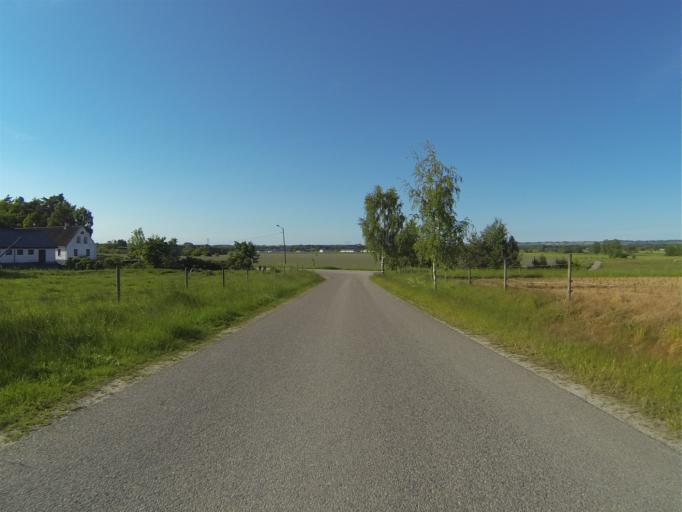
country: SE
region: Skane
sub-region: Lunds Kommun
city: Genarp
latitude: 55.7091
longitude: 13.3699
